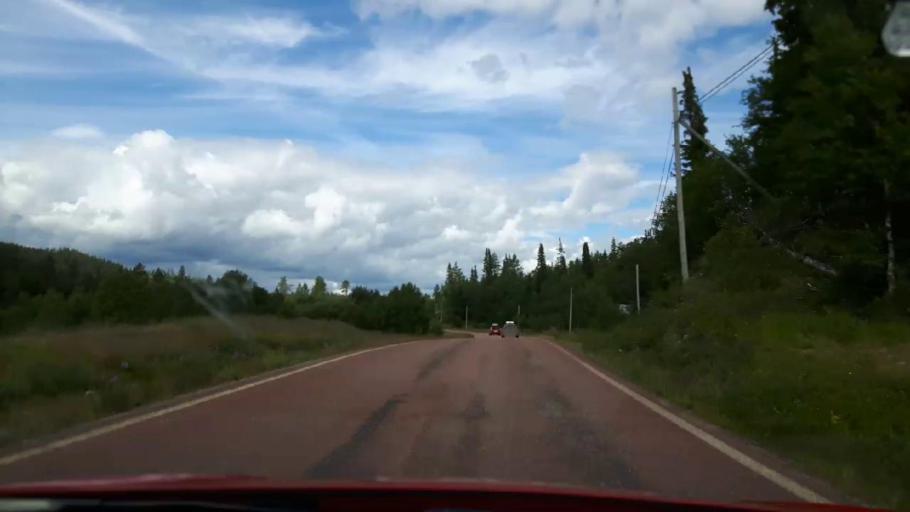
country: NO
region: Hedmark
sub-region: Trysil
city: Innbygda
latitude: 61.9980
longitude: 12.9807
